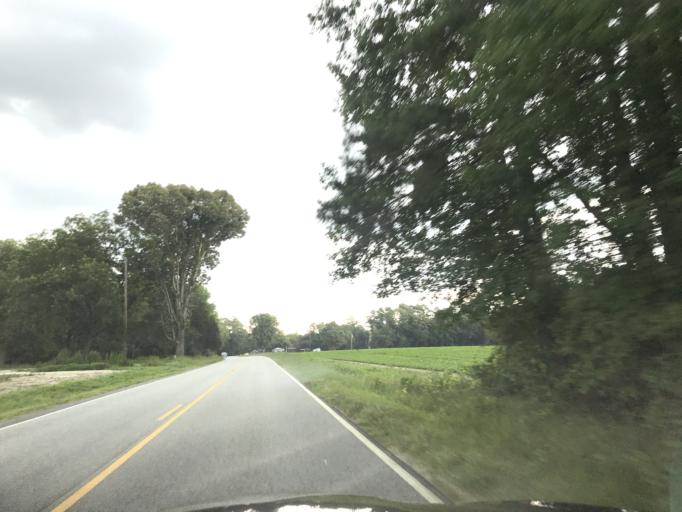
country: US
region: North Carolina
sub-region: Johnston County
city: Wilsons Mills
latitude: 35.5426
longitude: -78.4156
